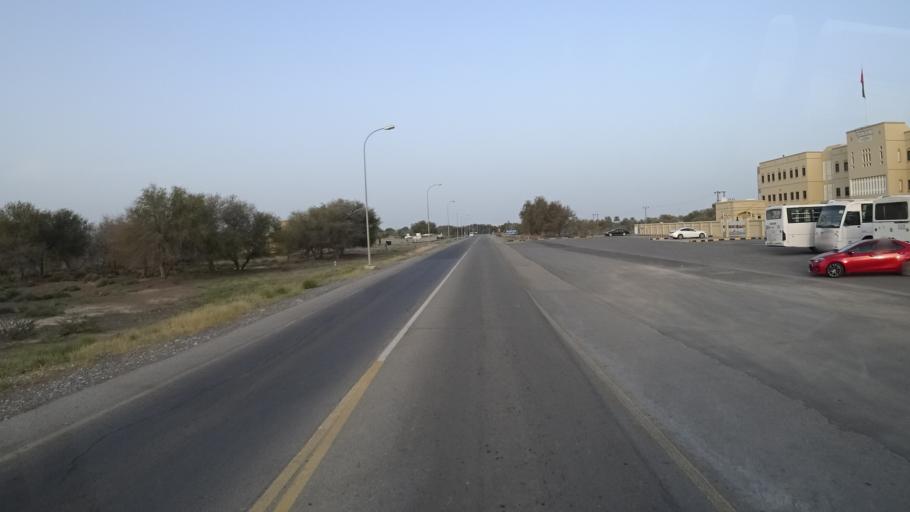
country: OM
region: Muhafazat Masqat
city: Muscat
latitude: 23.2054
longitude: 58.9572
